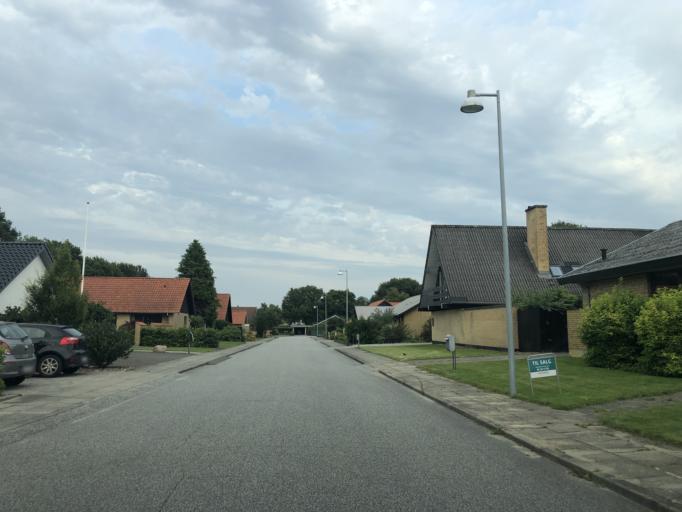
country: DK
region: Central Jutland
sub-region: Herning Kommune
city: Herning
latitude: 56.1483
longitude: 8.9519
